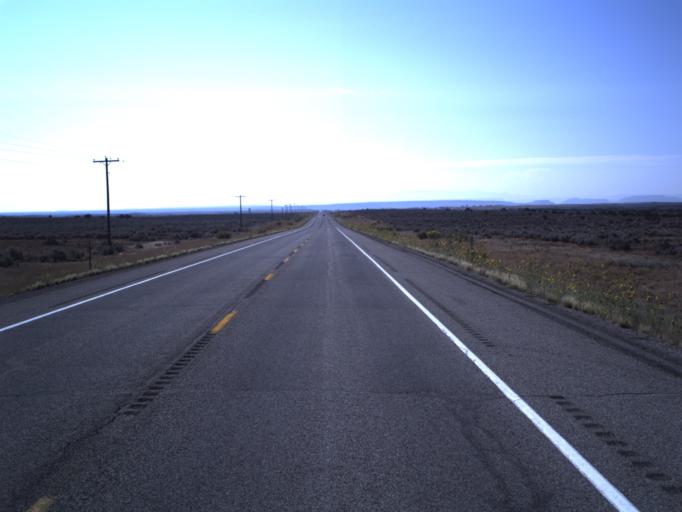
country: US
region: Utah
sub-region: San Juan County
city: Blanding
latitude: 37.5093
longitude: -109.4911
